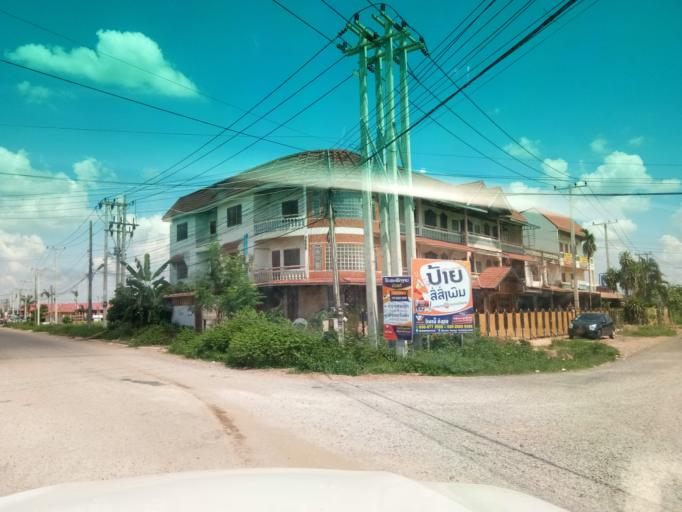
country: LA
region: Savannahkhet
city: Savannakhet
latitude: 16.5796
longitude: 104.7472
